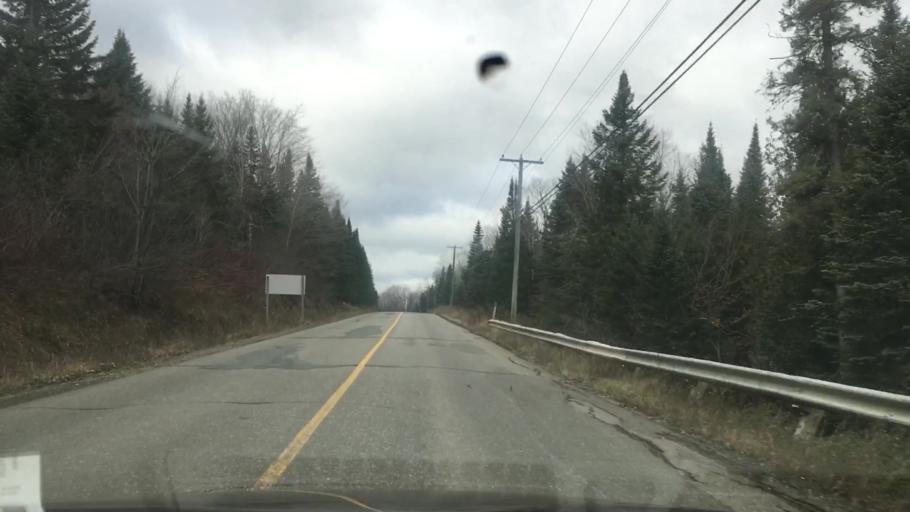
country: US
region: Maine
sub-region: Aroostook County
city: Fort Fairfield
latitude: 46.7505
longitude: -67.7236
